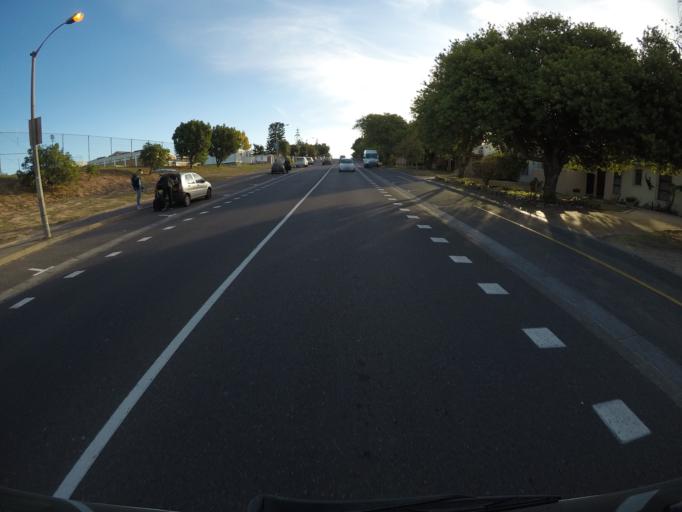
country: ZA
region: Western Cape
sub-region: City of Cape Town
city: Kraaifontein
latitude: -33.8623
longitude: 18.6631
